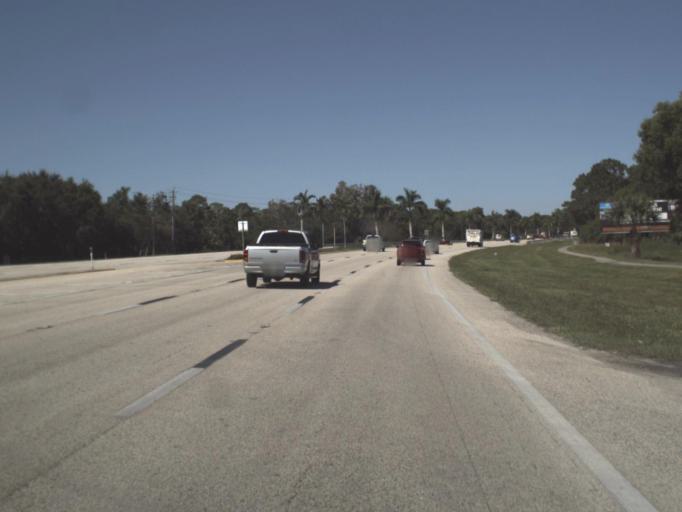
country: US
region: Florida
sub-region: Lee County
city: San Carlos Park
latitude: 26.4663
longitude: -81.8327
